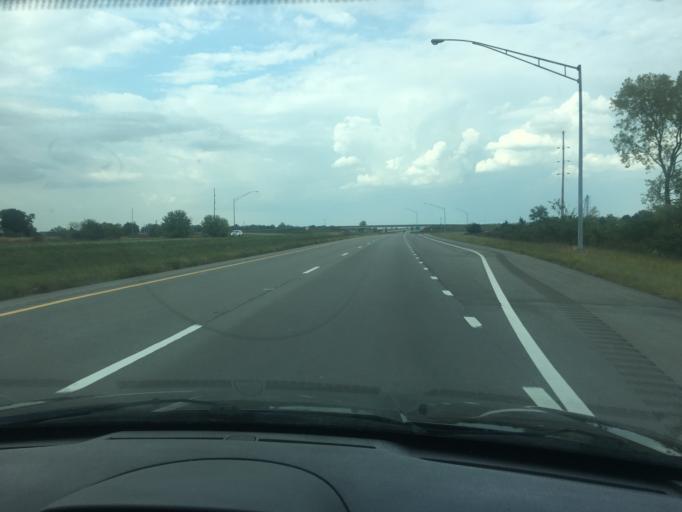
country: US
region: Ohio
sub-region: Clark County
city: Northridge
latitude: 40.0232
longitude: -83.8060
